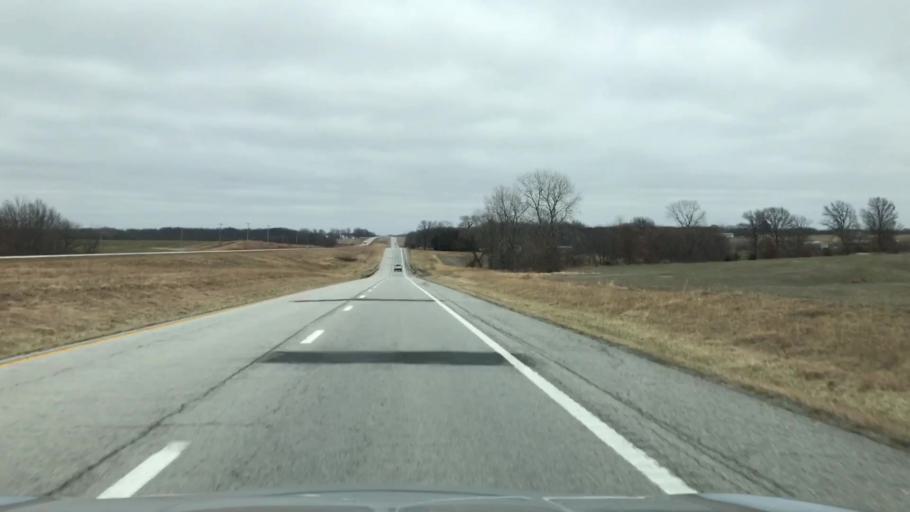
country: US
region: Missouri
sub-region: Linn County
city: Linneus
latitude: 39.7776
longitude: -93.2780
